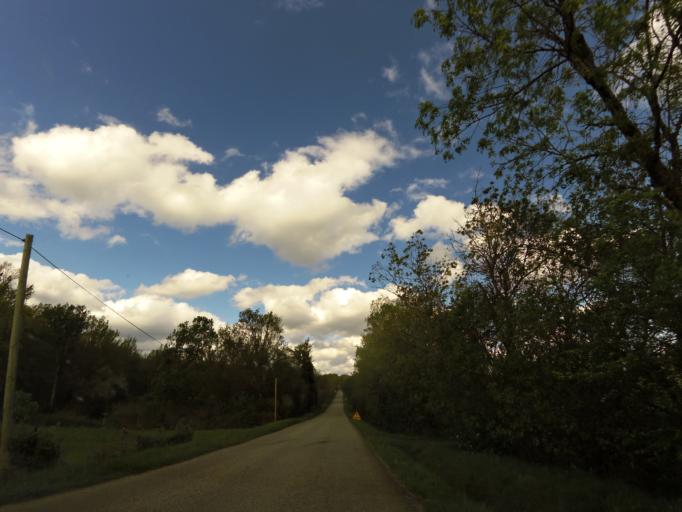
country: FR
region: Languedoc-Roussillon
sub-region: Departement de l'Aude
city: Saint-Martin-Lalande
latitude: 43.3400
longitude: 2.0546
